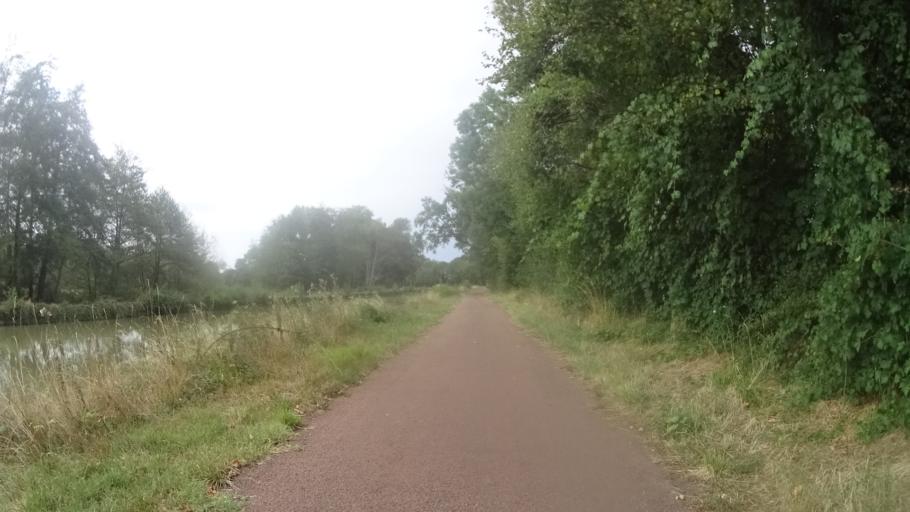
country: FR
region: Bourgogne
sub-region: Departement de la Nievre
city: Imphy
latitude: 46.9226
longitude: 3.2386
